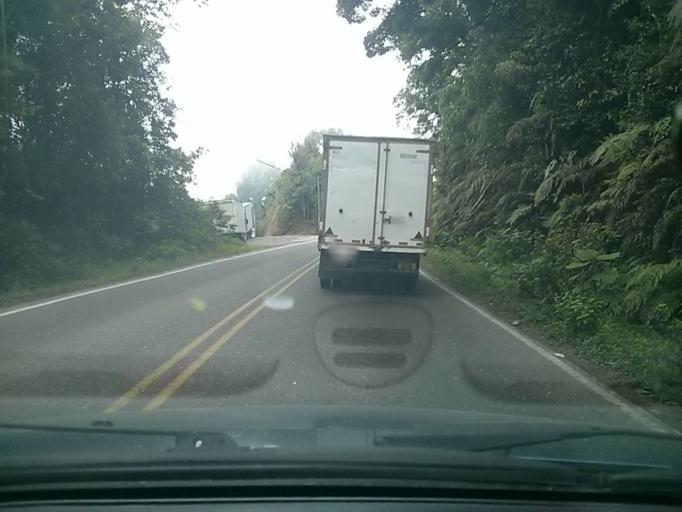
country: CR
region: Cartago
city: Tobosi
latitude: 9.7405
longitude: -83.9526
